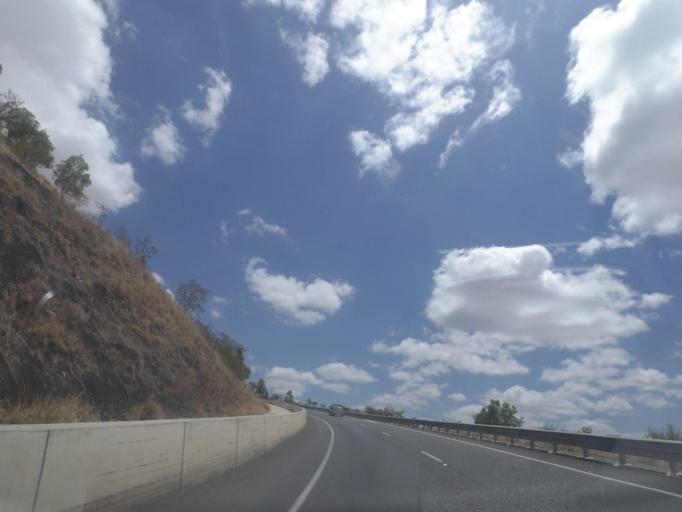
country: AU
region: Queensland
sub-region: Toowoomba
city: East Toowoomba
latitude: -27.5694
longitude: 151.9822
